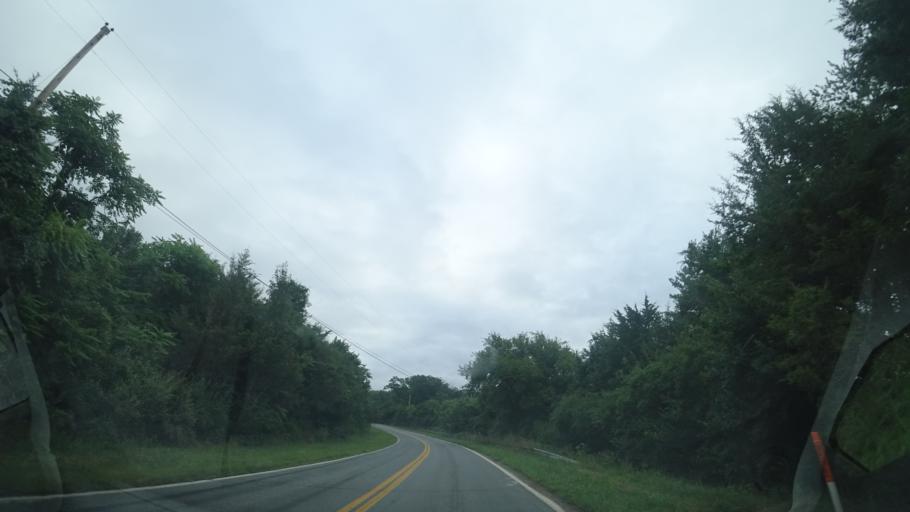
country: US
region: Virginia
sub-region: Loudoun County
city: University Center
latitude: 39.0851
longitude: -77.4127
